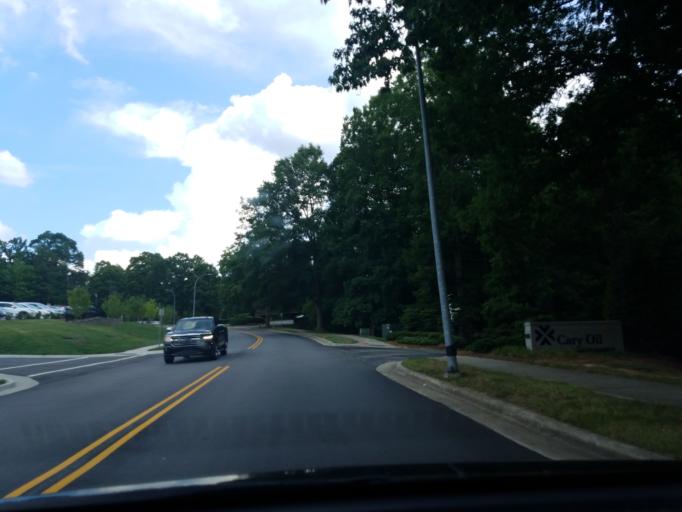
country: US
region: North Carolina
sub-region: Wake County
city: Apex
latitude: 35.7359
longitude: -78.8088
